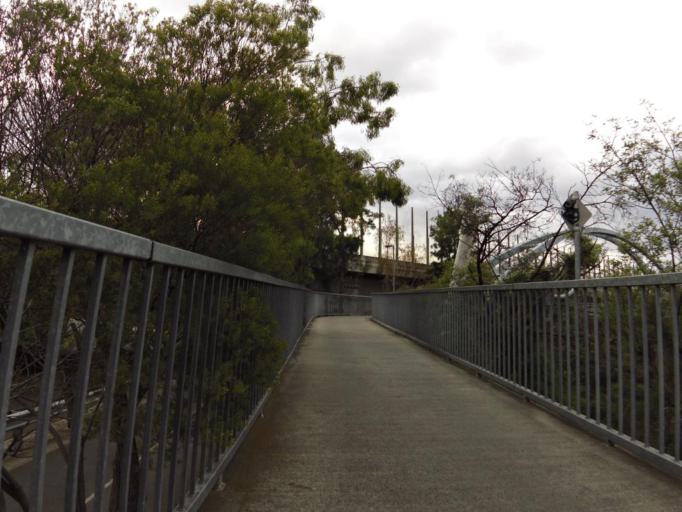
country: AU
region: Victoria
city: Toorak
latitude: -37.8341
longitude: 145.0239
